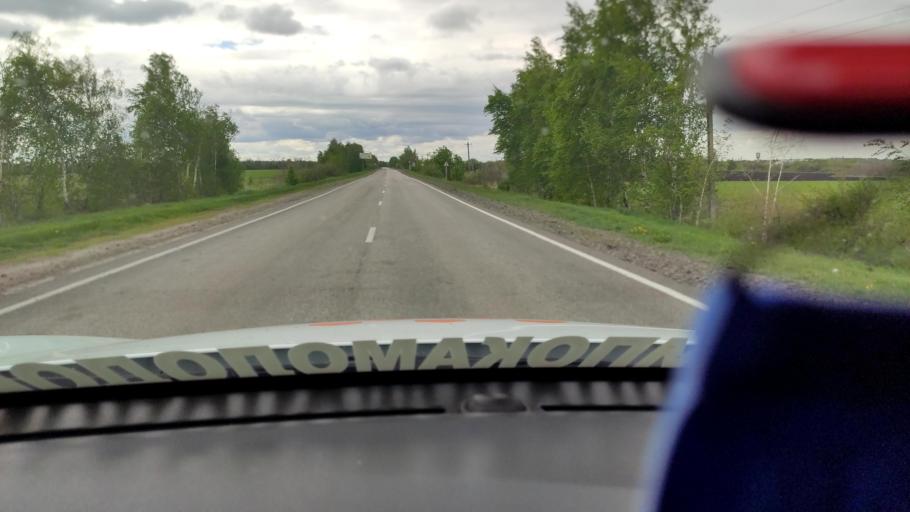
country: RU
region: Voronezj
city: Imeni Pervogo Maya
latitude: 50.7745
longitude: 39.3851
